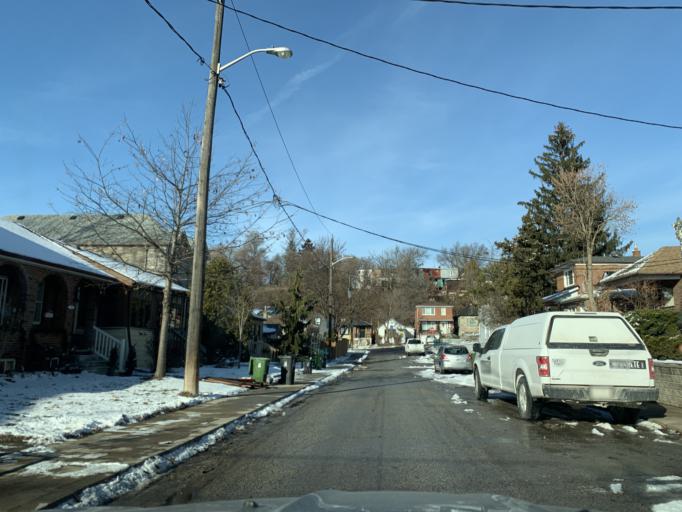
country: CA
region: Ontario
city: Toronto
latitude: 43.6815
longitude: -79.4851
